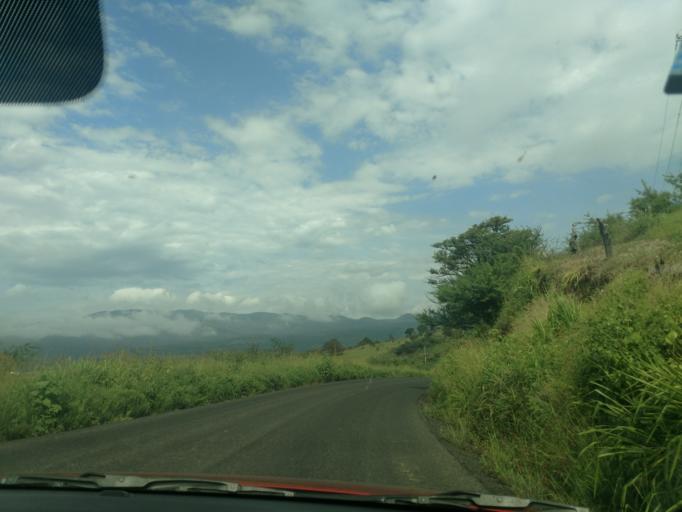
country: MX
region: Jalisco
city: El Salto
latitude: 20.4317
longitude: -104.4761
